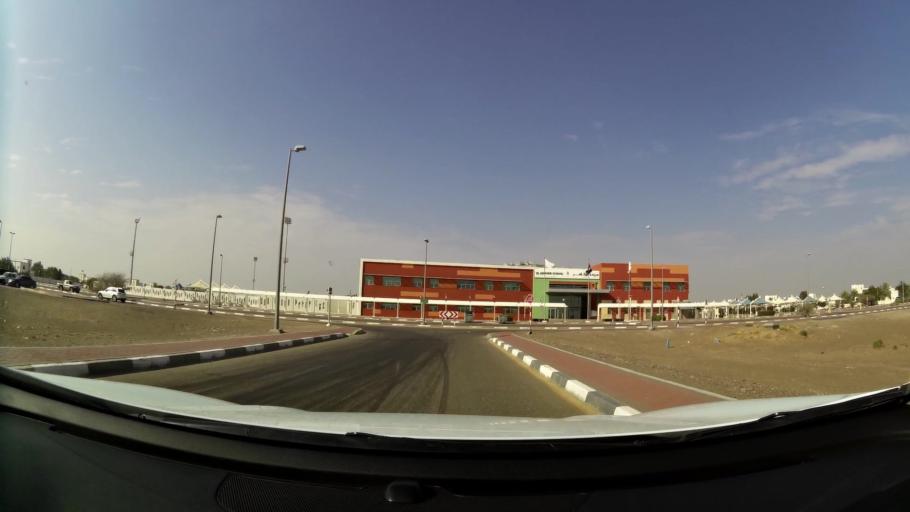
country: AE
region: Abu Dhabi
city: Al Ain
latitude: 24.0711
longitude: 55.8671
